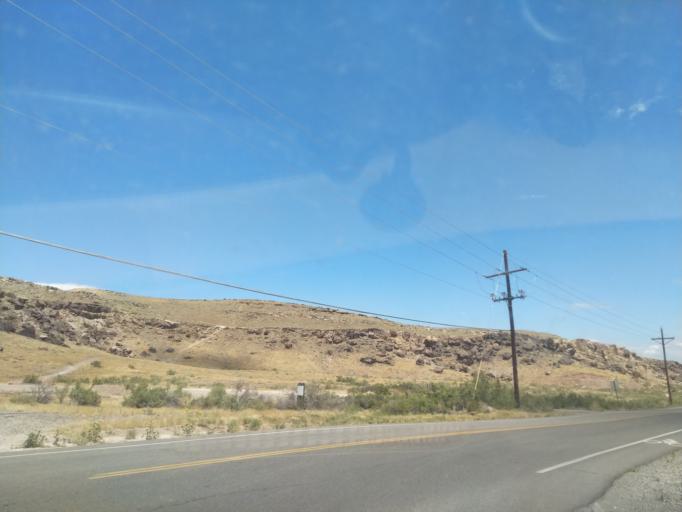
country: US
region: Colorado
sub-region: Mesa County
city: Redlands
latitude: 39.0726
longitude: -108.6492
